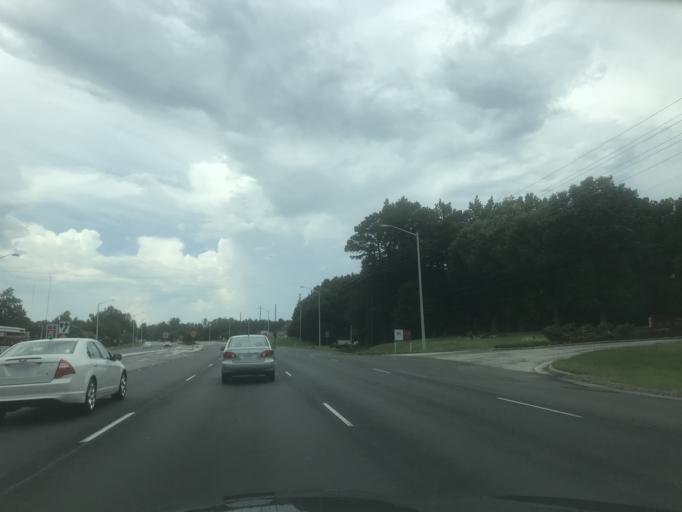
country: US
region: North Carolina
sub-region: Johnston County
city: Clayton
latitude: 35.6542
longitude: -78.4738
